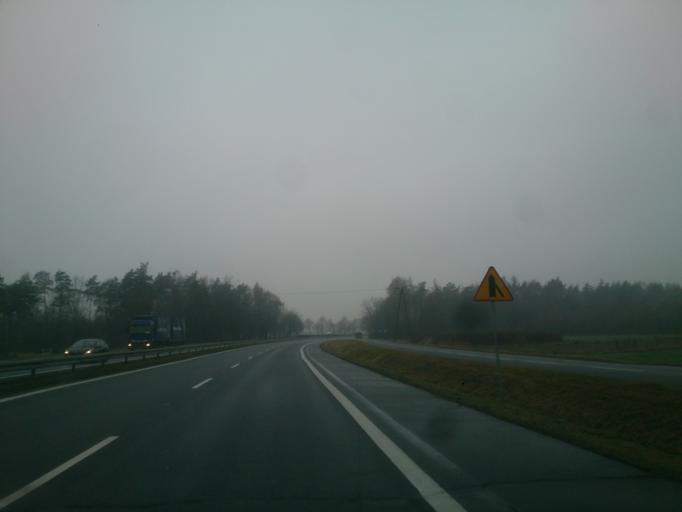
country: PL
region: Masovian Voivodeship
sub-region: Powiat nowodworski
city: Zakroczym
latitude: 52.4523
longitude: 20.5866
